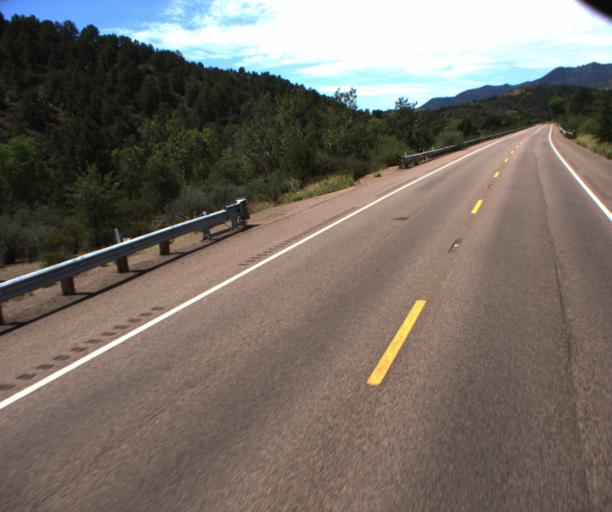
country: US
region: Arizona
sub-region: Gila County
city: Globe
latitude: 33.5668
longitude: -110.6692
